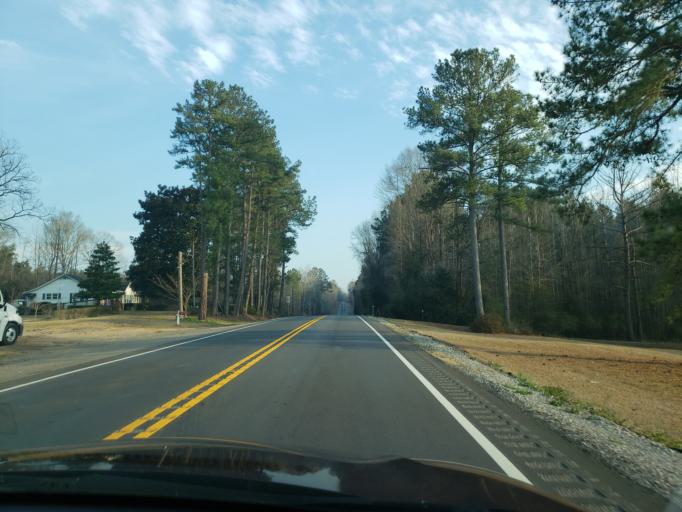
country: US
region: Alabama
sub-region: Hale County
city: Greensboro
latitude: 32.8186
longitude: -87.5992
